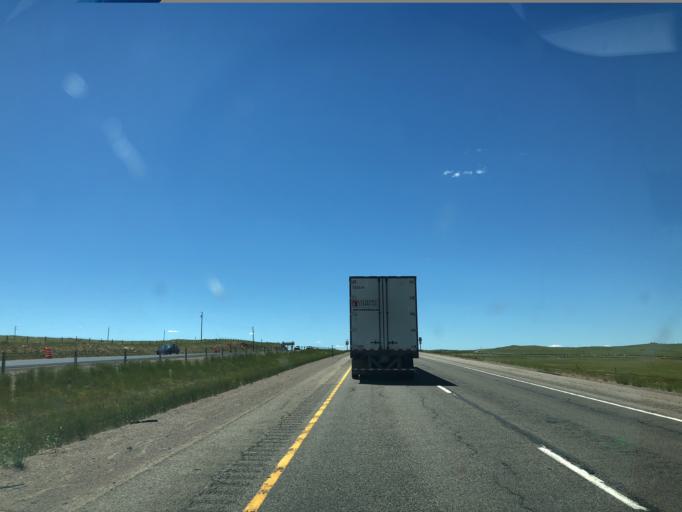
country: US
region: Wyoming
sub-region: Laramie County
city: Cheyenne
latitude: 41.0965
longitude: -105.1870
